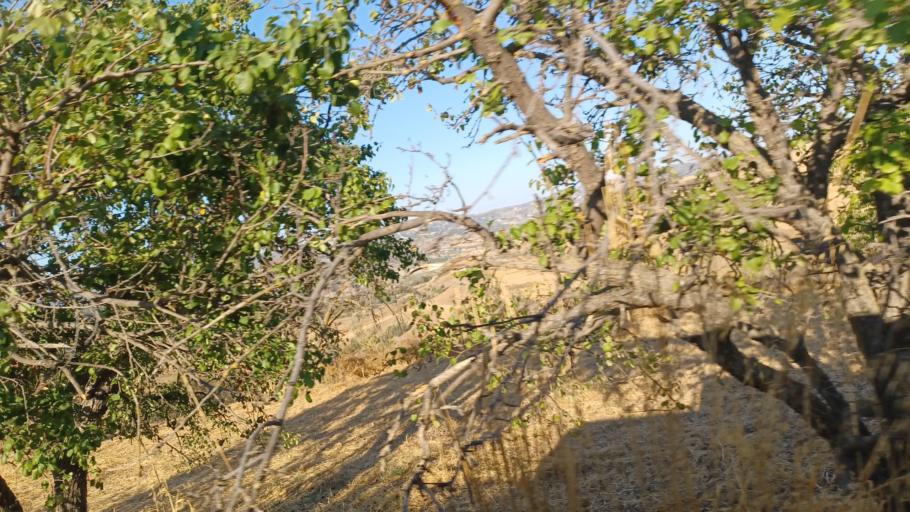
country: CY
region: Pafos
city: Tala
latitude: 34.9136
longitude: 32.5257
